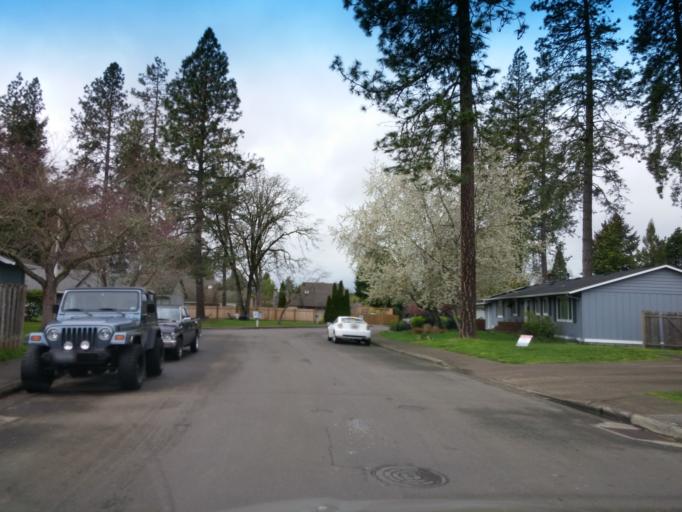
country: US
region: Oregon
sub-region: Washington County
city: Aloha
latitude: 45.5105
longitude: -122.8596
